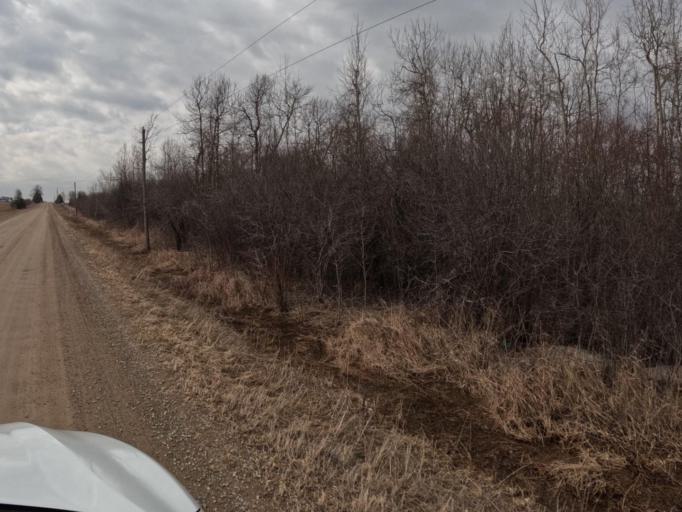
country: CA
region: Ontario
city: Orangeville
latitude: 43.9352
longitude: -80.1890
